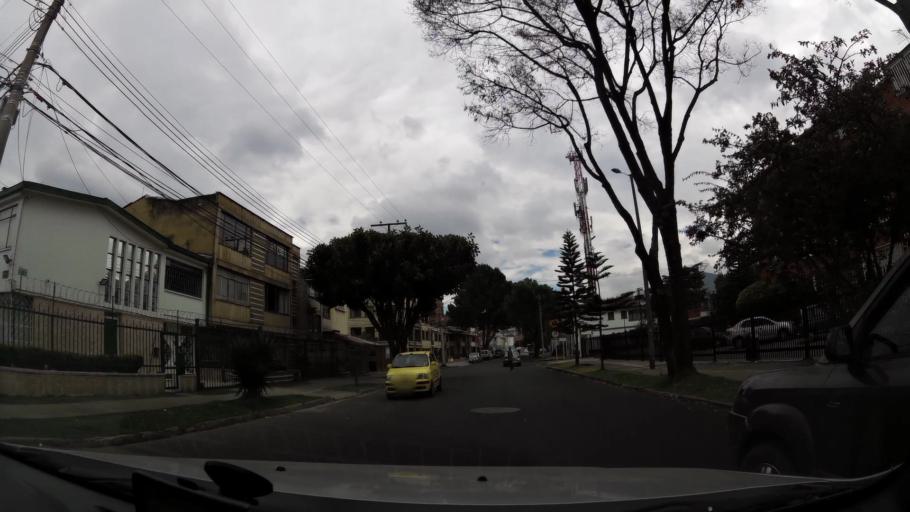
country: CO
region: Bogota D.C.
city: Bogota
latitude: 4.6263
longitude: -74.0842
